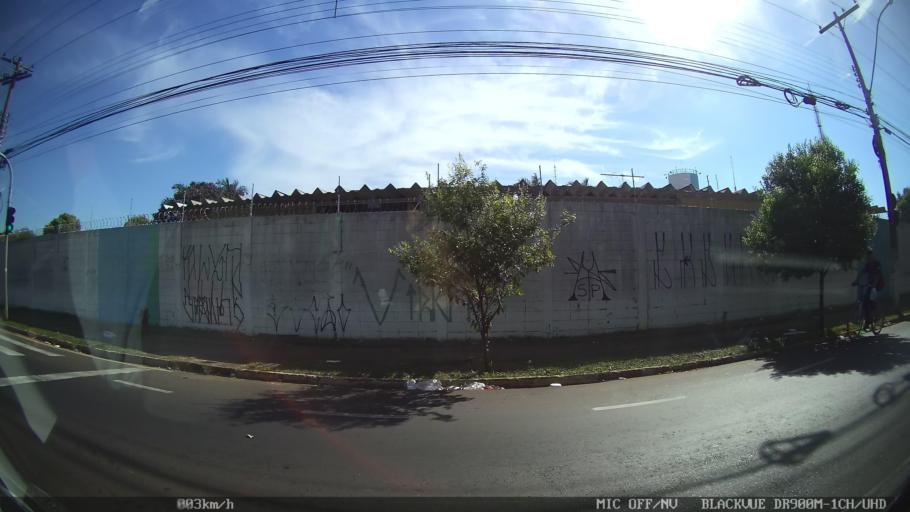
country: BR
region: Sao Paulo
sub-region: Franca
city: Franca
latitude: -20.5070
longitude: -47.3997
